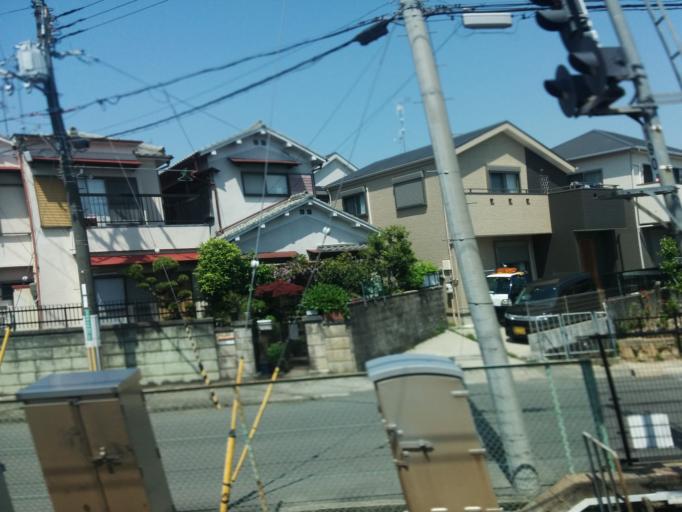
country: JP
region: Osaka
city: Ibaraki
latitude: 34.8294
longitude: 135.5866
